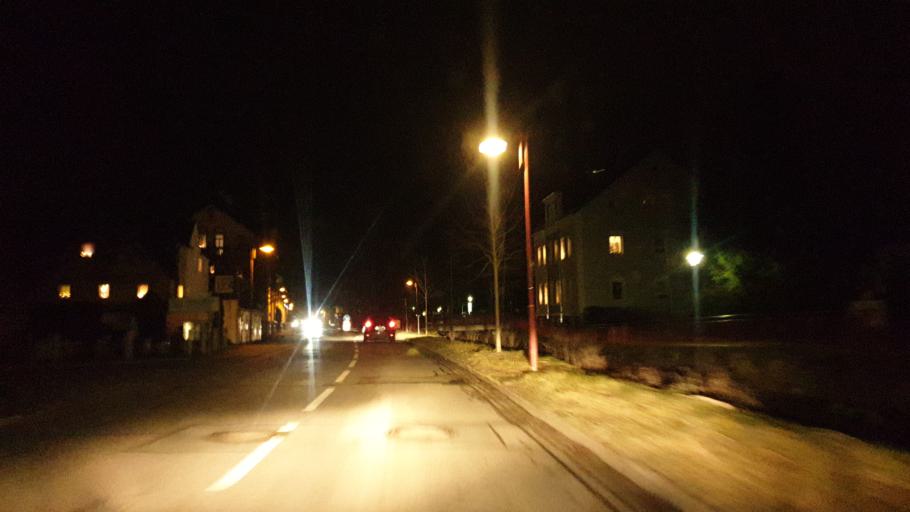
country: DE
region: Saxony
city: Lugau
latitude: 50.7208
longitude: 12.7496
